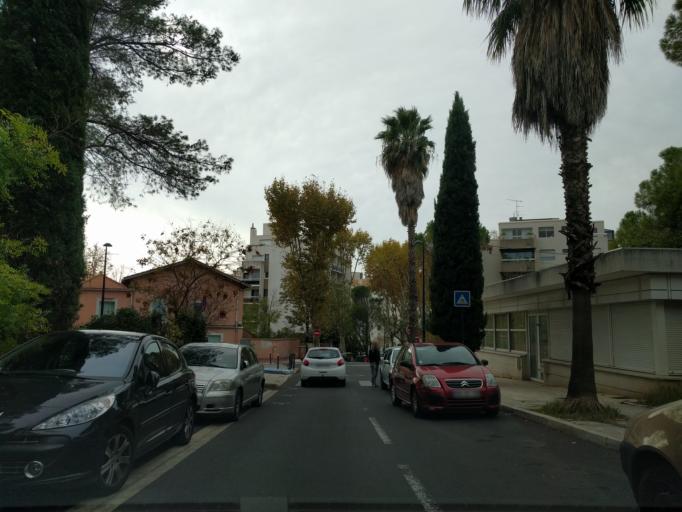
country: FR
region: Languedoc-Roussillon
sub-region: Departement de l'Herault
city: Montpellier
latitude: 43.6295
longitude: 3.8727
